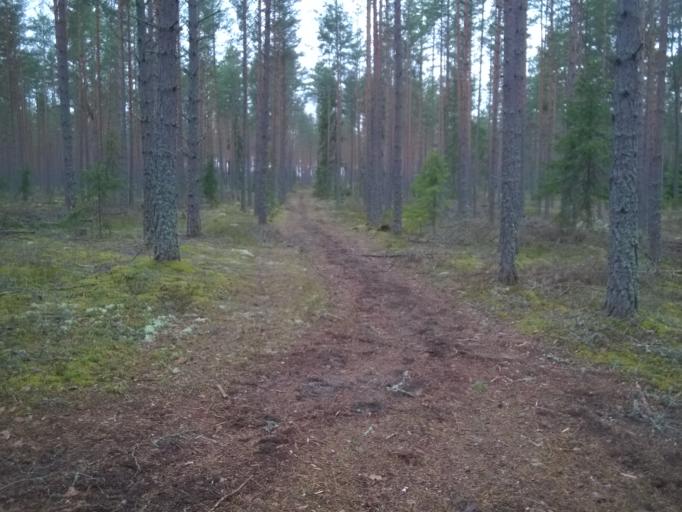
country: SE
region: Uppsala
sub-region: Osthammars Kommun
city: Bjorklinge
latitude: 60.1587
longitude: 17.5007
